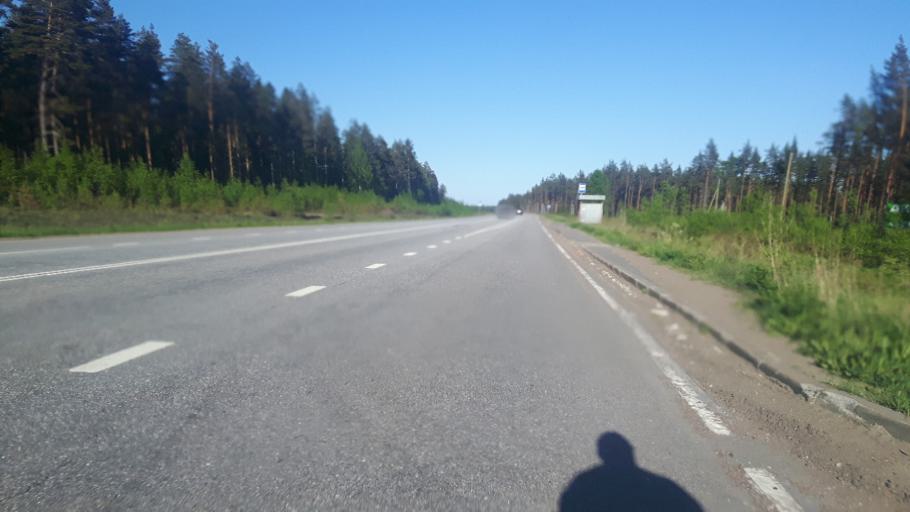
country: RU
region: Leningrad
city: Molodezhnoye
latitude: 60.1717
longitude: 29.3100
